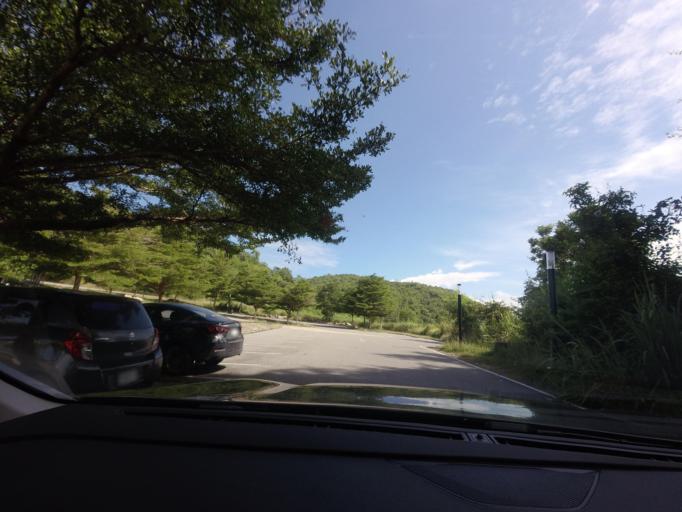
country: TH
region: Prachuap Khiri Khan
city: Hua Hin
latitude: 12.4973
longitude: 99.9466
